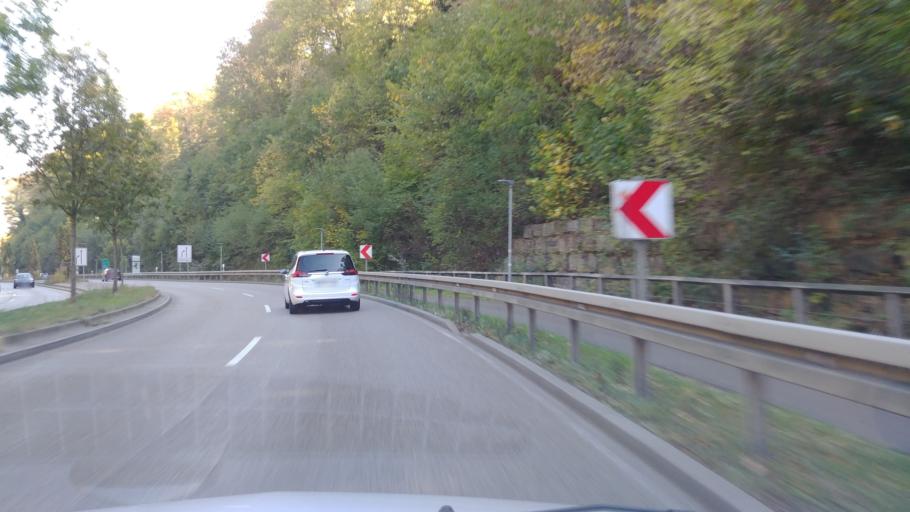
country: DE
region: Baden-Wuerttemberg
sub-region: Regierungsbezirk Stuttgart
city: Schwaebisch Hall
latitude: 49.1100
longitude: 9.7242
